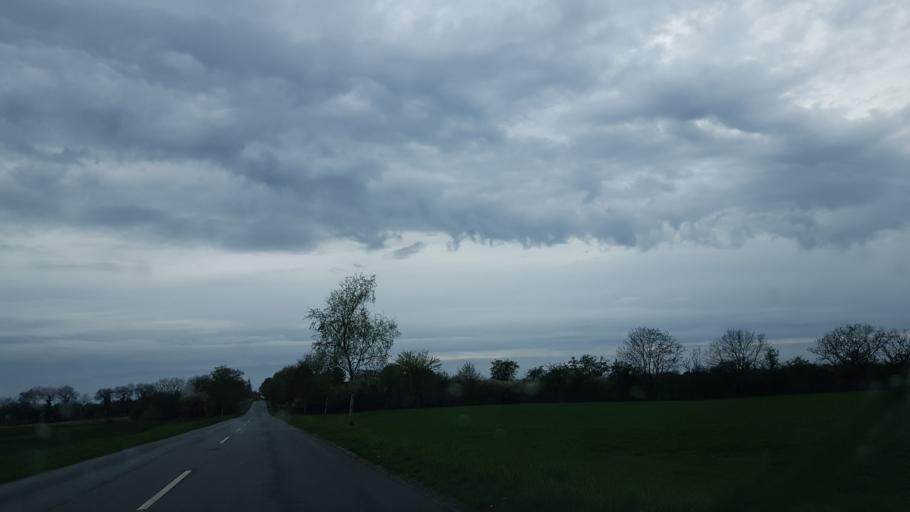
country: DK
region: South Denmark
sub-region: Kolding Kommune
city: Lunderskov
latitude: 55.4633
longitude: 9.3798
